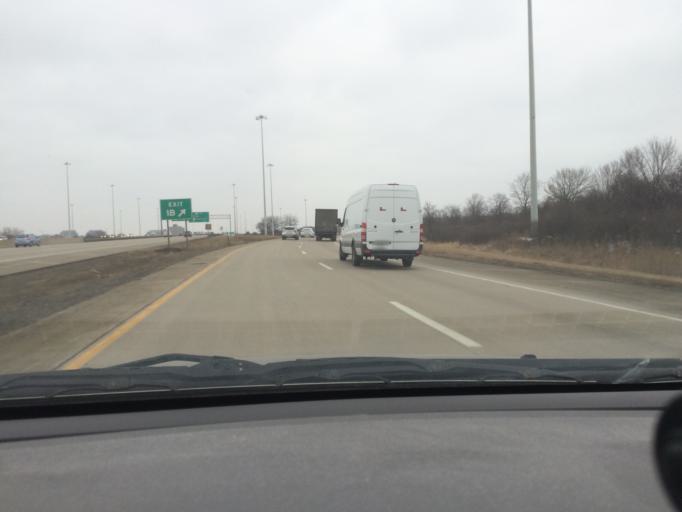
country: US
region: Illinois
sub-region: Cook County
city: Hoffman Estates
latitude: 42.0323
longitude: -88.0306
